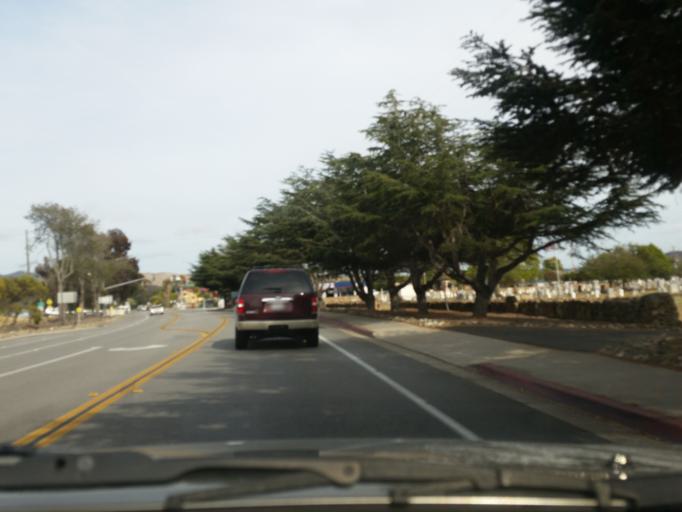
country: US
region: California
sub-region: San Luis Obispo County
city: Arroyo Grande
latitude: 35.1236
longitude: -120.5932
